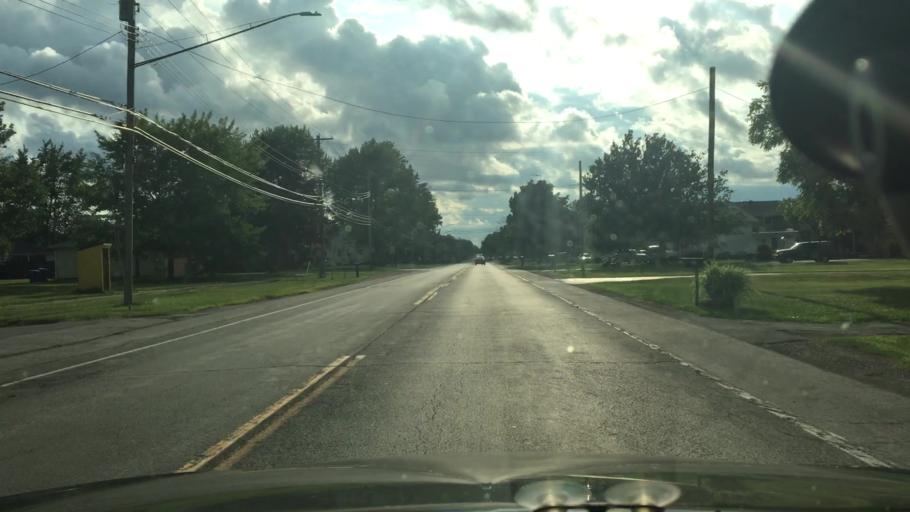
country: US
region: New York
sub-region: Erie County
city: Cheektowaga
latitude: 42.8393
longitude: -78.7301
